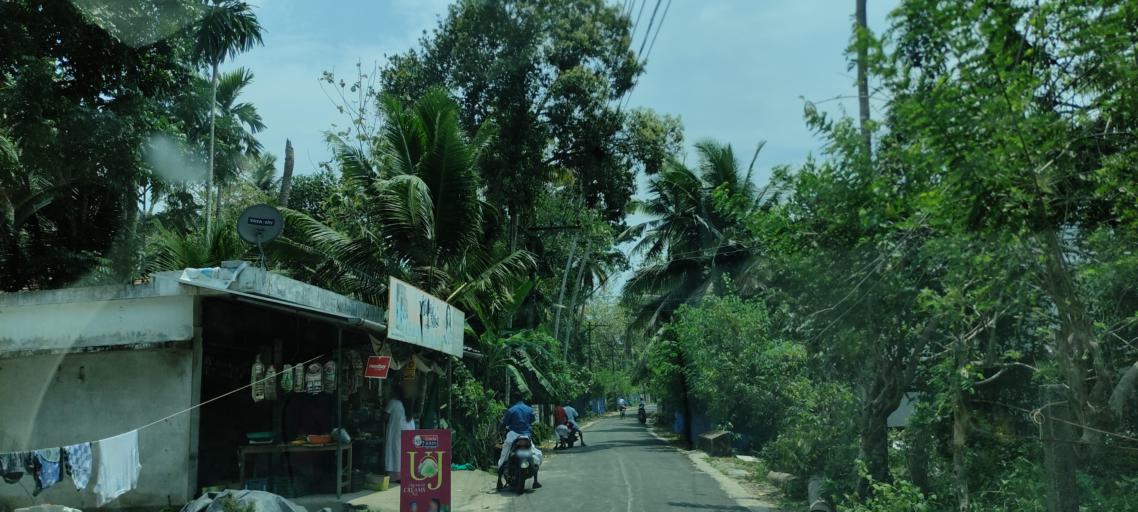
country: IN
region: Kerala
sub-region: Alappuzha
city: Vayalar
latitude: 9.7210
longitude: 76.3408
